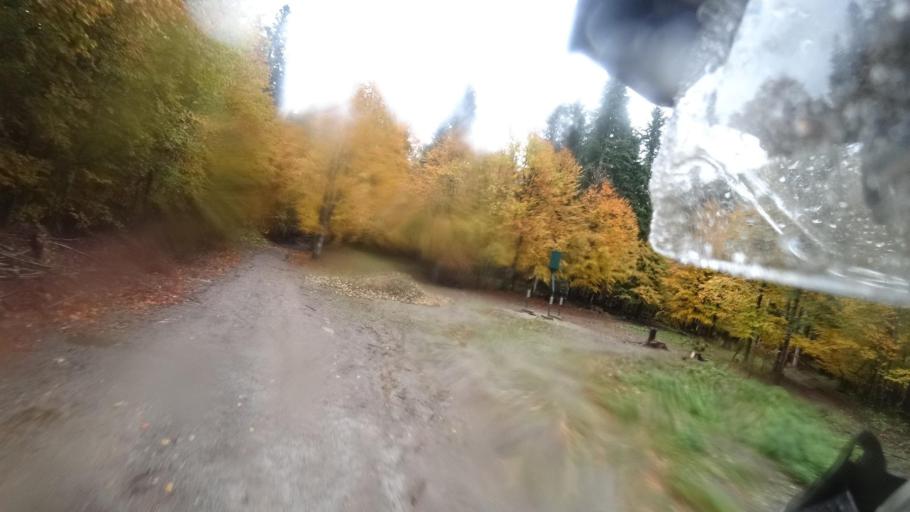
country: HR
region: Primorsko-Goranska
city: Vrbovsko
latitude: 45.3399
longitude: 15.0702
